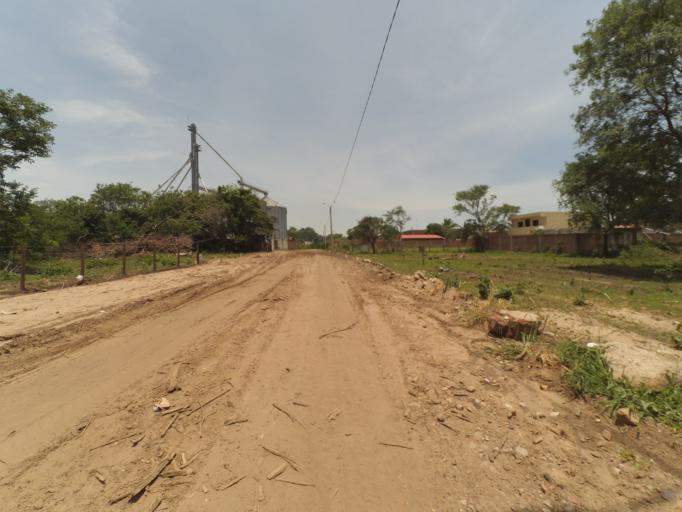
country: BO
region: Santa Cruz
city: Santa Cruz de la Sierra
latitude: -17.8359
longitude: -63.2439
